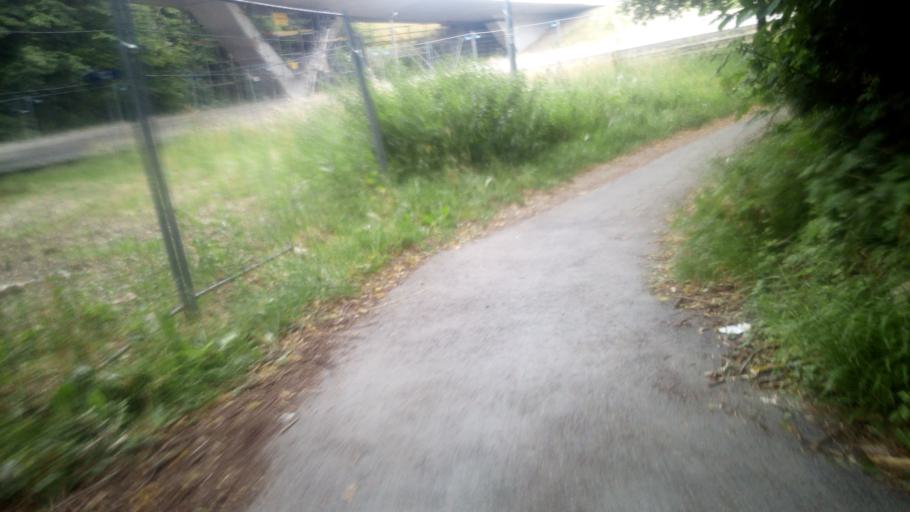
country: CH
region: Vaud
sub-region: Ouest Lausannois District
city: Chavannes
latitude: 46.5234
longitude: 6.5747
